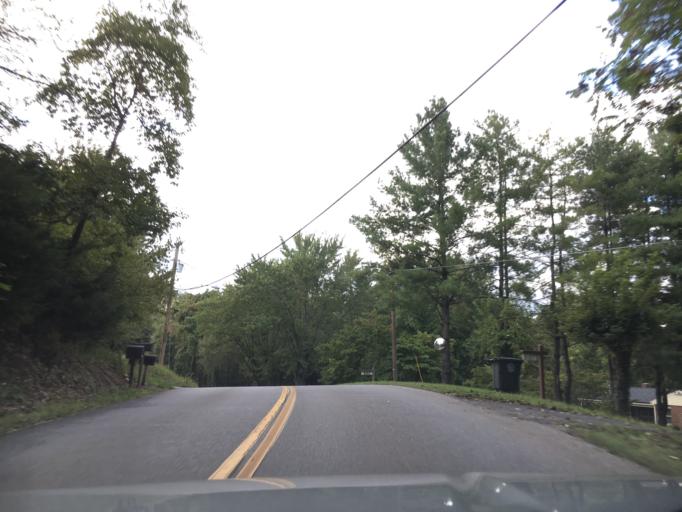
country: US
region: Virginia
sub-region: City of Lynchburg
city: West Lynchburg
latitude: 37.3791
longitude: -79.1533
